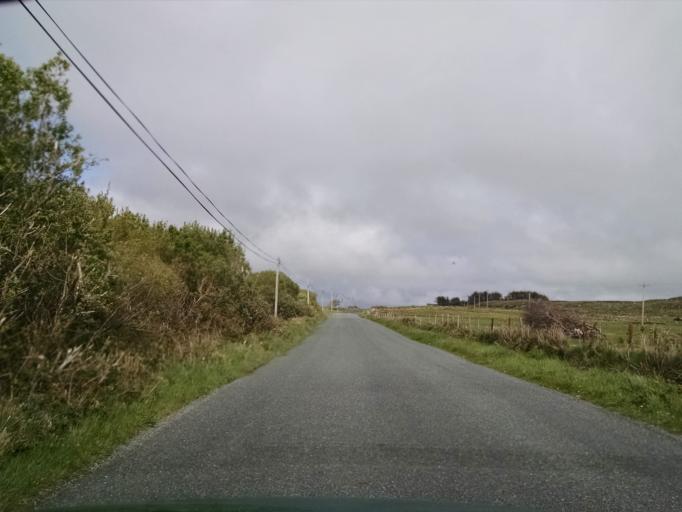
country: IE
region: Connaught
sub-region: County Galway
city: Clifden
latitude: 53.7376
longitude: -9.8559
